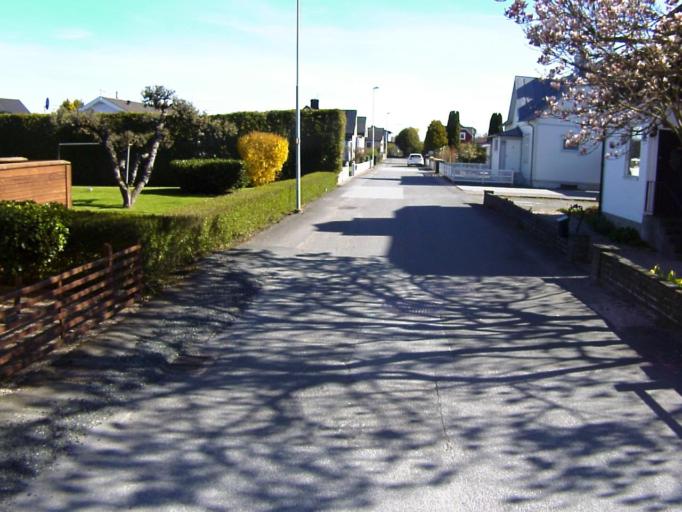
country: SE
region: Skane
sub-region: Kristianstads Kommun
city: Kristianstad
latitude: 56.0129
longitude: 14.1516
